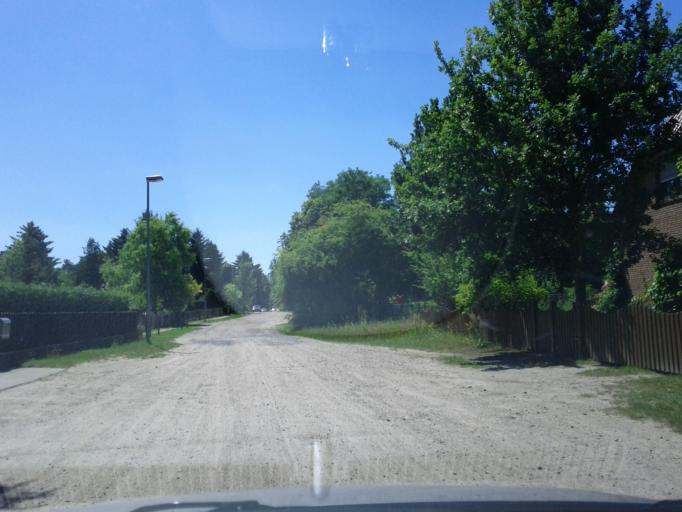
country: DE
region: Brandenburg
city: Schoneiche
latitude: 52.4683
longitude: 13.7176
